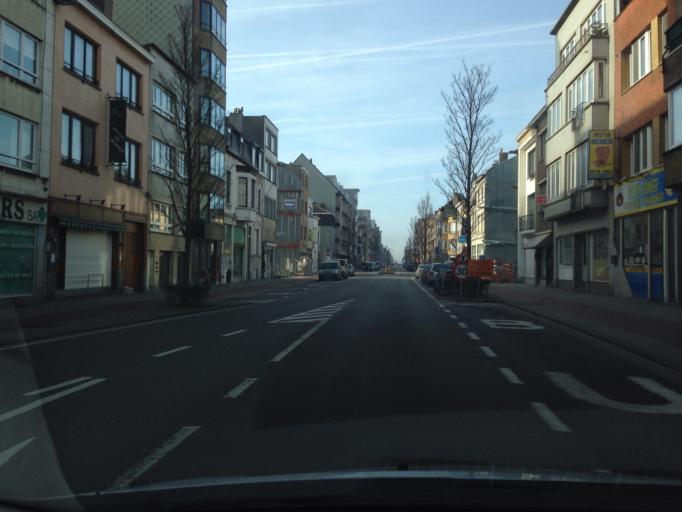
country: BE
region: Flanders
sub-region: Provincie West-Vlaanderen
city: Ostend
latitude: 51.2178
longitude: 2.9074
